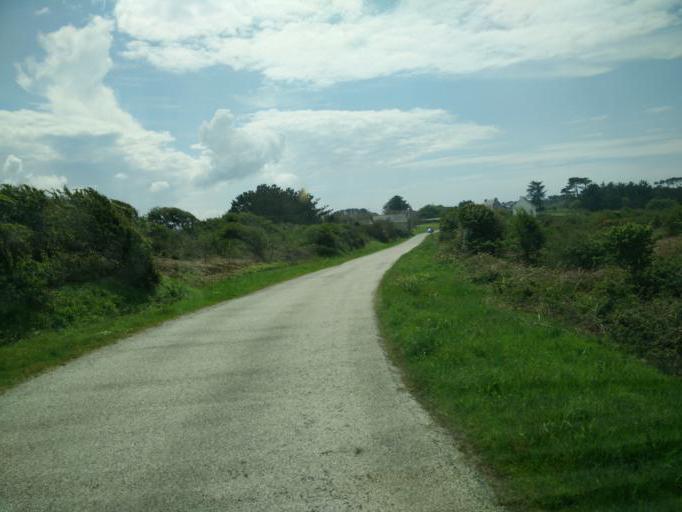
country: FR
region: Brittany
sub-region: Departement du Finistere
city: Roscanvel
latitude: 48.3270
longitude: -4.5691
